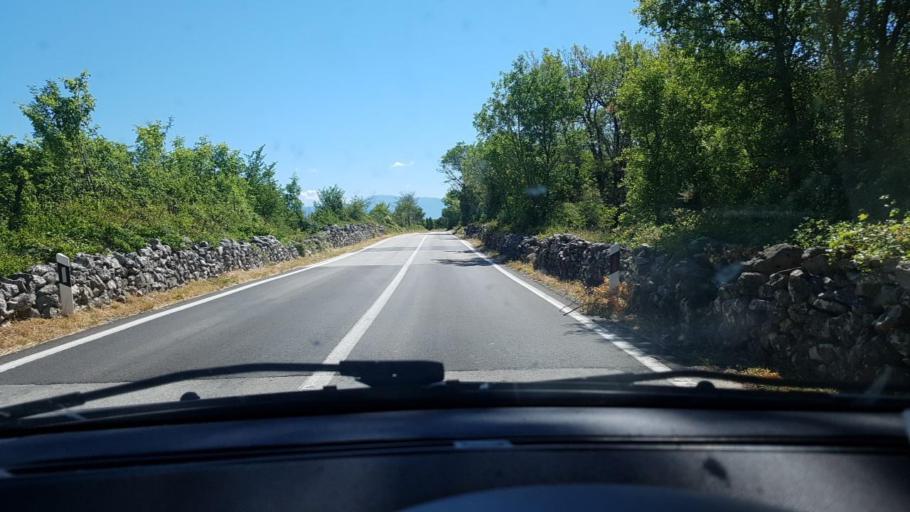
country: HR
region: Sibensko-Kniniska
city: Kistanje
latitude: 44.0172
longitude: 16.0181
